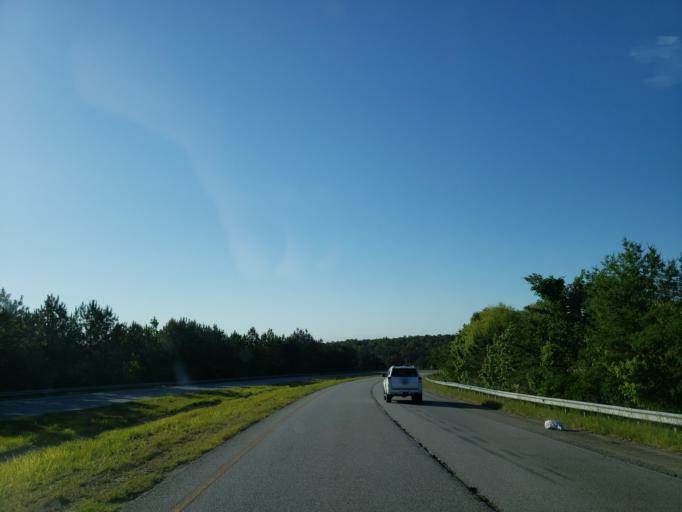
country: US
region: Georgia
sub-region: Haralson County
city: Buchanan
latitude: 33.9138
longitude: -85.2445
